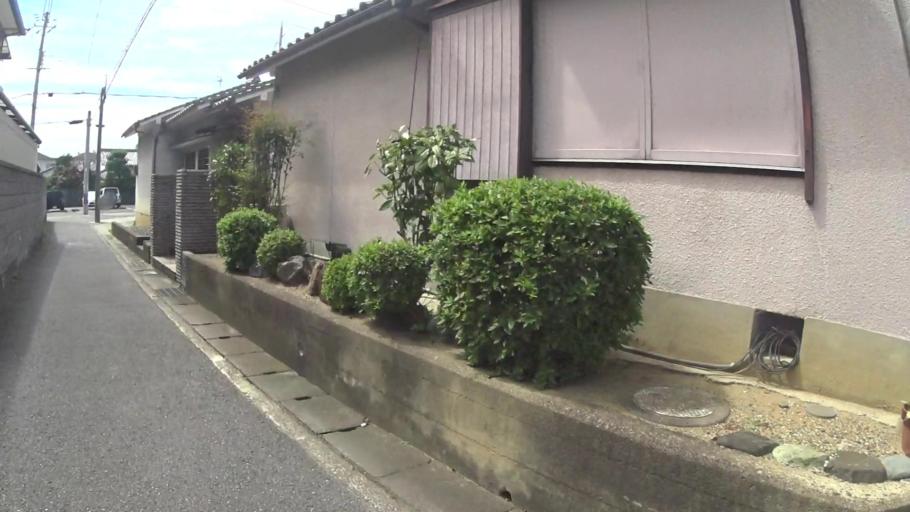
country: JP
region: Kyoto
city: Muko
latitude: 34.9422
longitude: 135.7064
